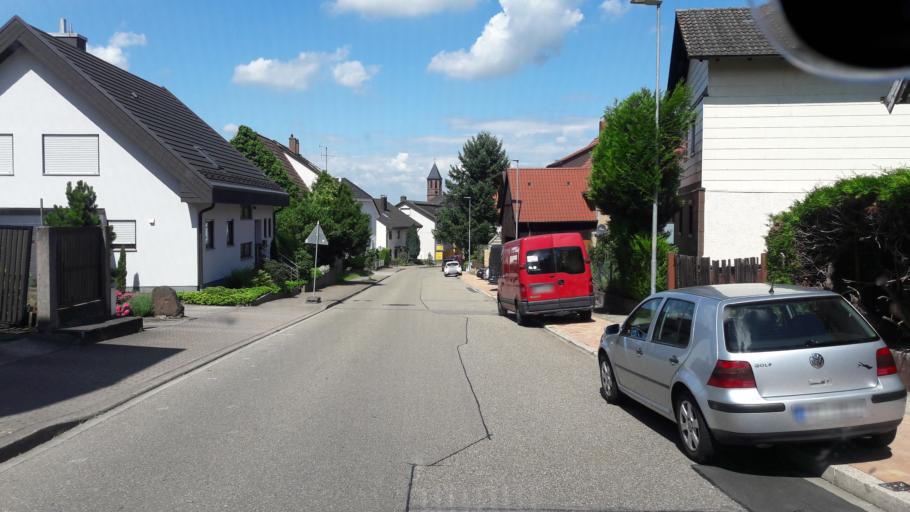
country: DE
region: Baden-Wuerttemberg
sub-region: Karlsruhe Region
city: Malsch
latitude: 48.8774
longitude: 8.3410
